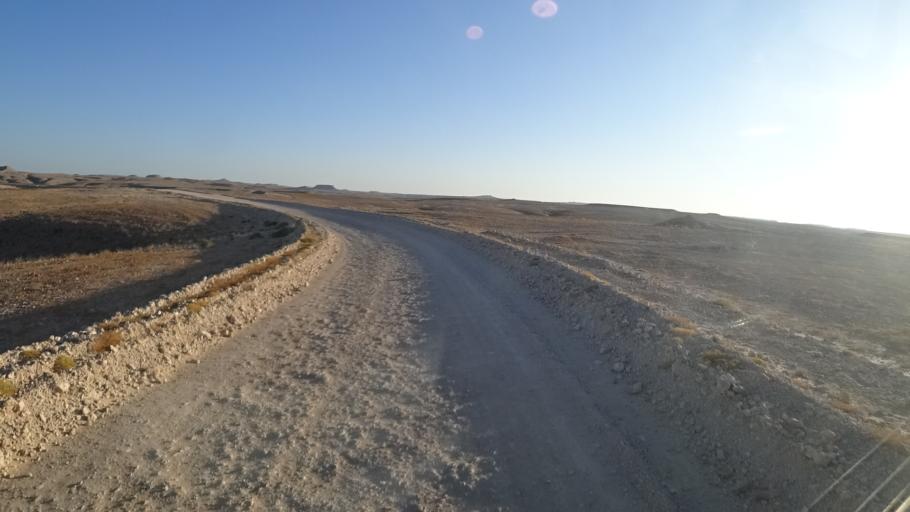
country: YE
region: Al Mahrah
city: Hawf
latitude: 17.1574
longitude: 53.3497
